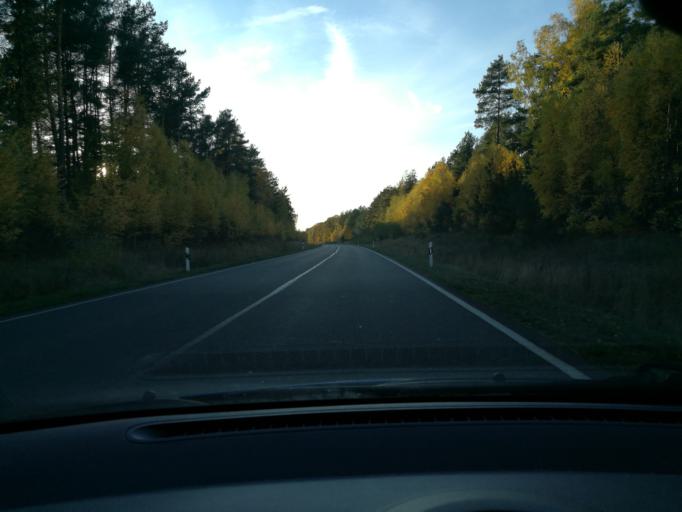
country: DE
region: Brandenburg
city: Perleberg
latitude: 53.0892
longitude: 11.8877
